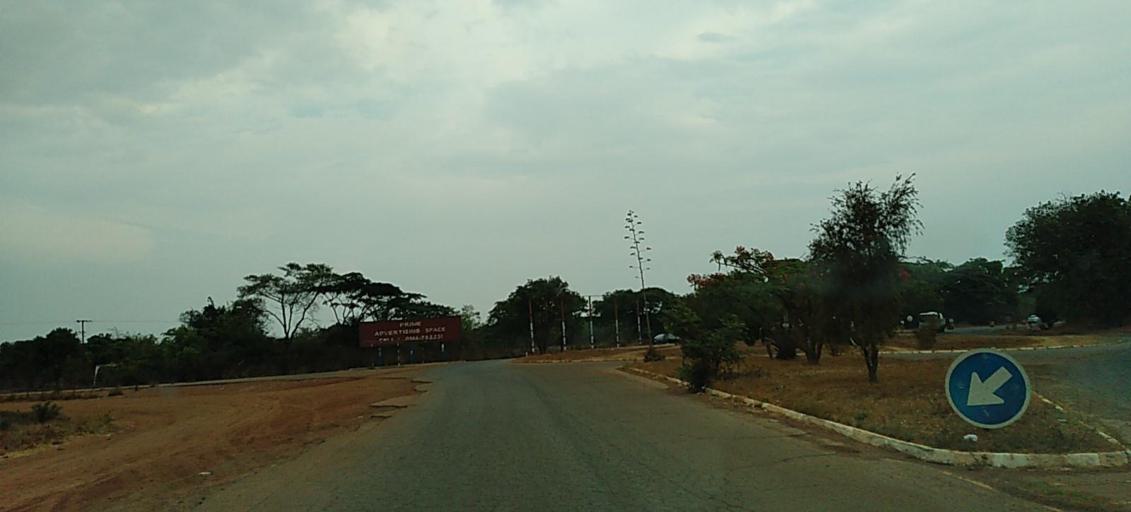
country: ZM
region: Copperbelt
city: Luanshya
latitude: -13.0478
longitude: 28.4657
